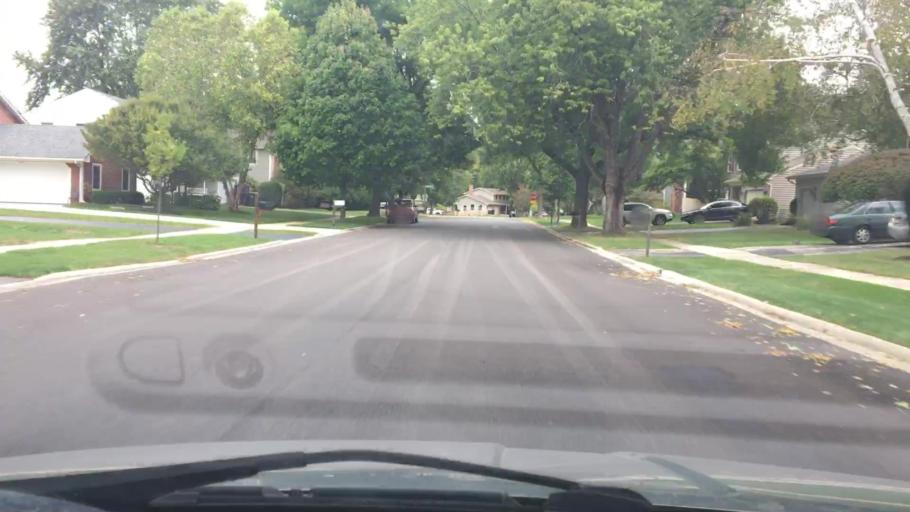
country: US
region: Illinois
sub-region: DuPage County
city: Naperville
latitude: 41.7371
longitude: -88.1363
